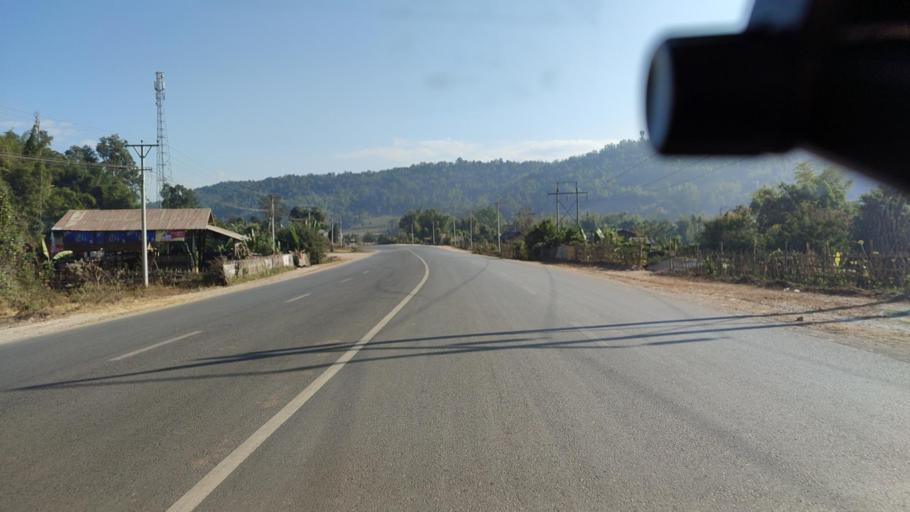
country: MM
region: Shan
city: Lashio
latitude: 23.1402
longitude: 97.8498
